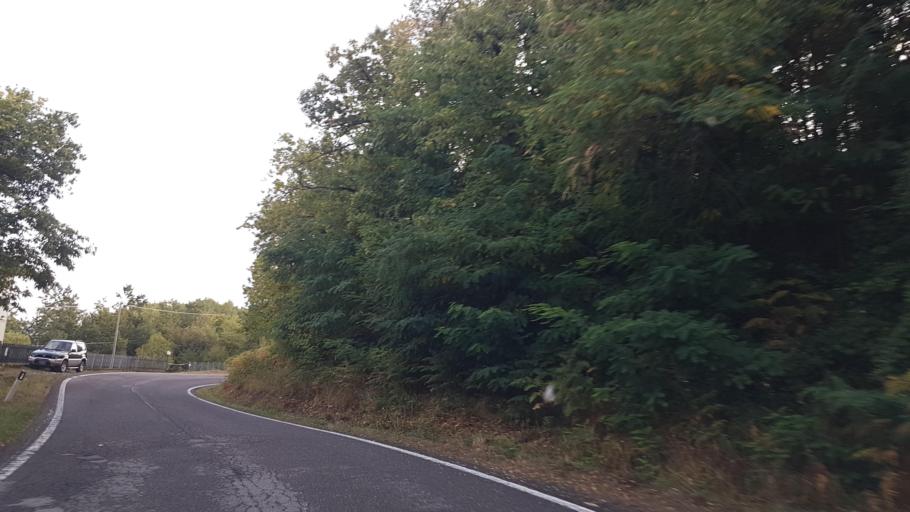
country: IT
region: Emilia-Romagna
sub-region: Provincia di Parma
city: Tornolo
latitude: 44.4449
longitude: 9.6372
